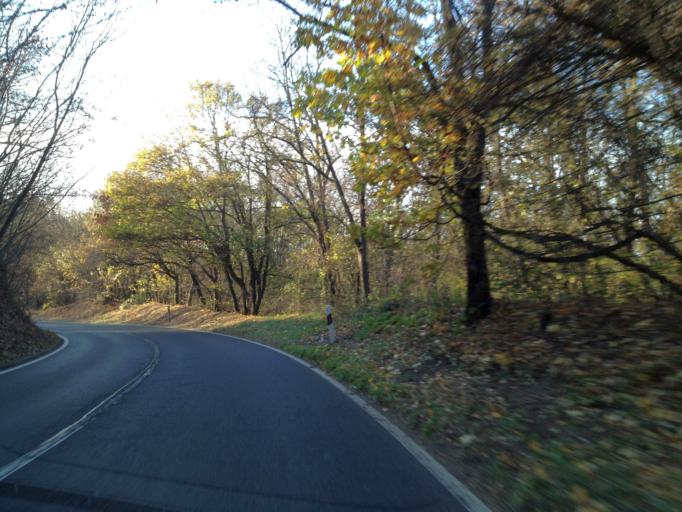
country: HU
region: Veszprem
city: Zirc
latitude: 47.3409
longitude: 17.8816
